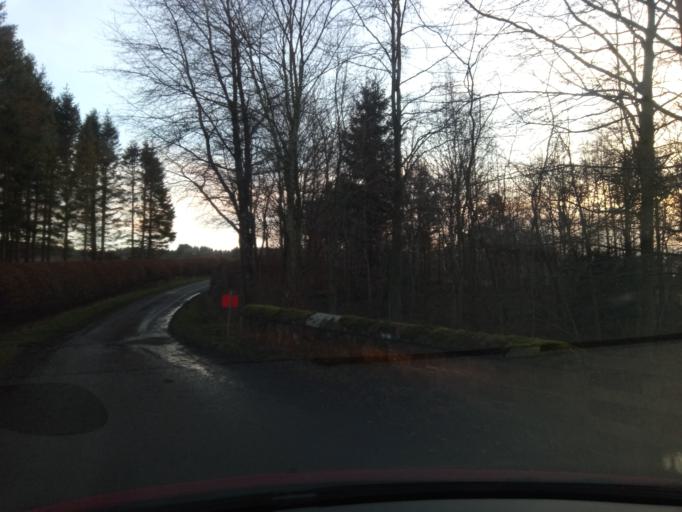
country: GB
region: Scotland
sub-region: The Scottish Borders
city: Saint Boswells
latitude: 55.5147
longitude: -2.6624
